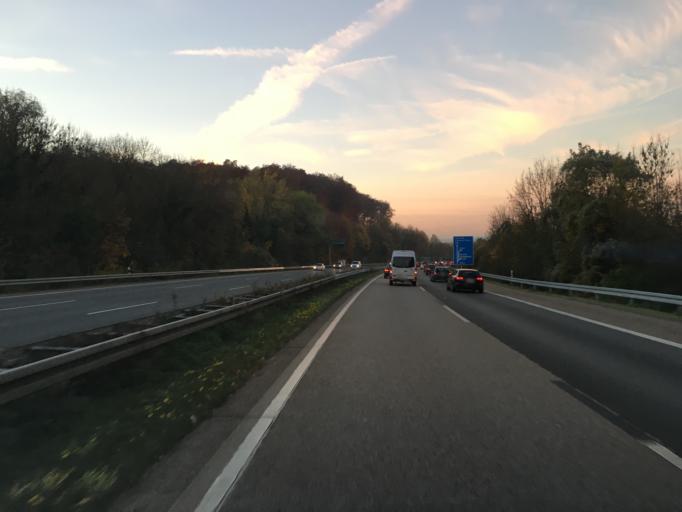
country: DE
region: North Rhine-Westphalia
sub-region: Regierungsbezirk Arnsberg
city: Hagen
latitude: 51.3584
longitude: 7.5163
